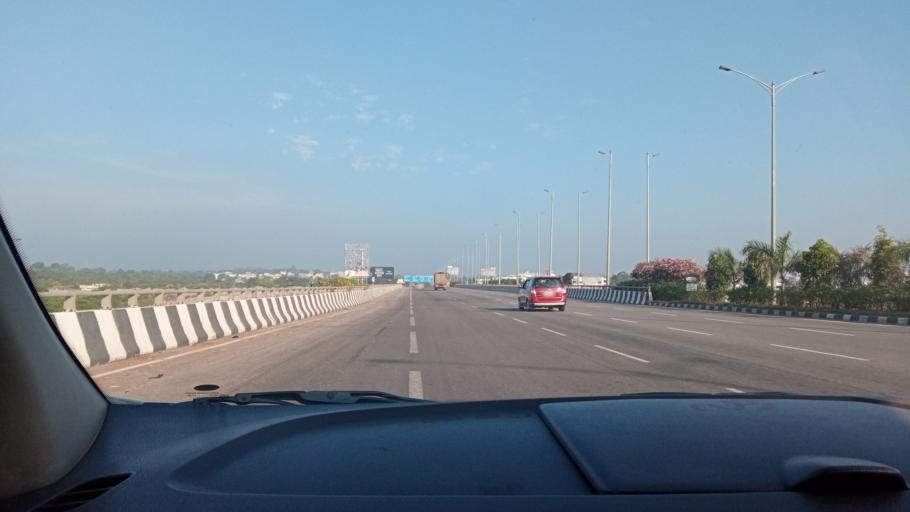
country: IN
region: Telangana
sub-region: Hyderabad
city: Hyderabad
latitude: 17.3266
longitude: 78.3736
